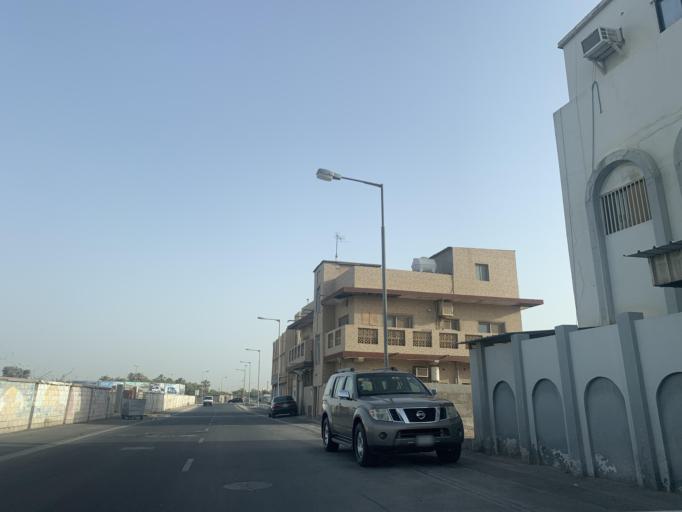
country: BH
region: Manama
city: Jidd Hafs
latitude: 26.2221
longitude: 50.5466
